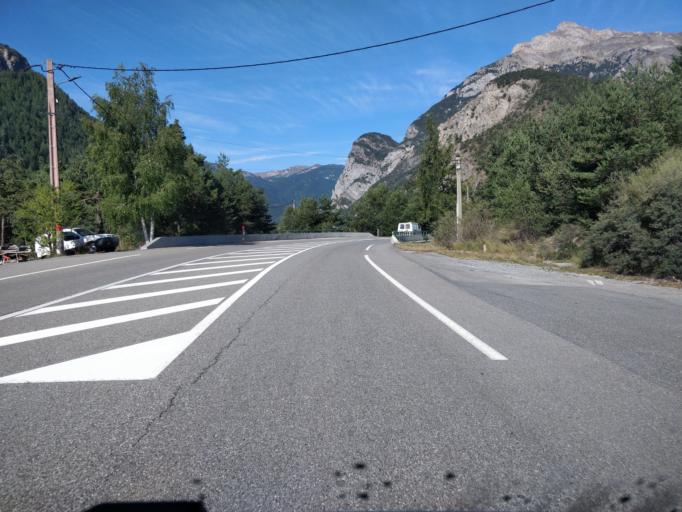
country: FR
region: Provence-Alpes-Cote d'Azur
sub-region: Departement des Alpes-de-Haute-Provence
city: Barcelonnette
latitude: 44.3997
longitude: 6.5311
